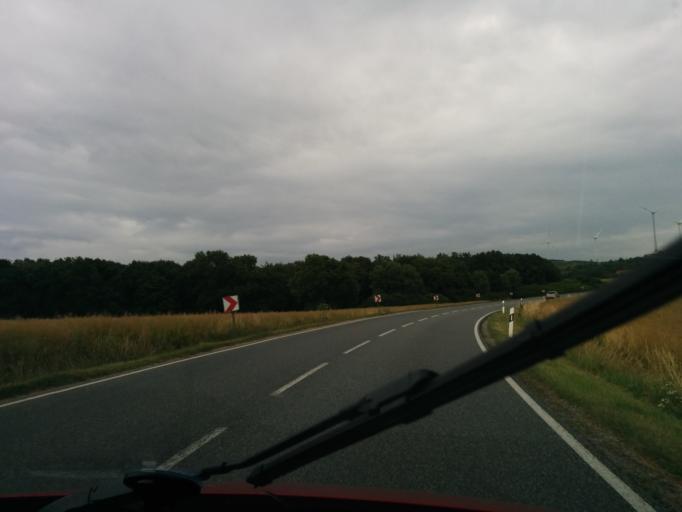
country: DE
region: Thuringia
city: Kleinfurra
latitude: 51.4447
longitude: 10.7879
